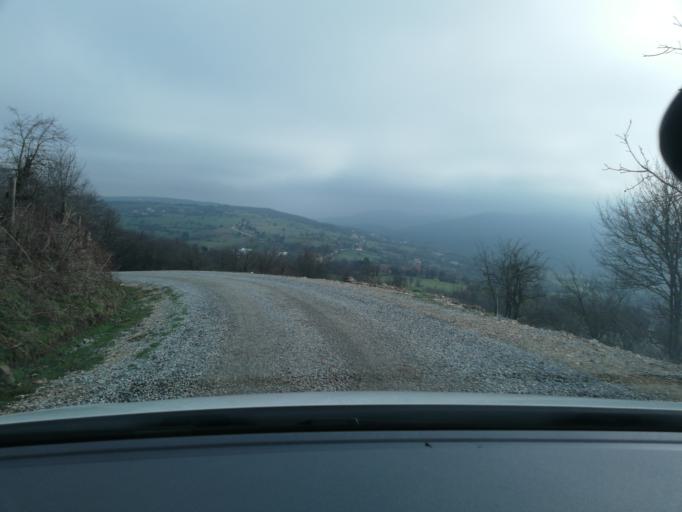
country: TR
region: Bolu
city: Bolu
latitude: 40.6674
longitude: 31.4615
